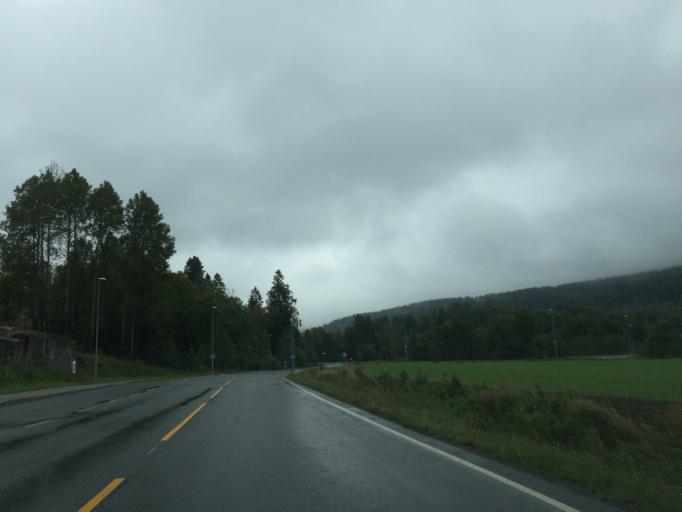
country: NO
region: Akershus
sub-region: Baerum
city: Lysaker
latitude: 59.9901
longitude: 10.6219
